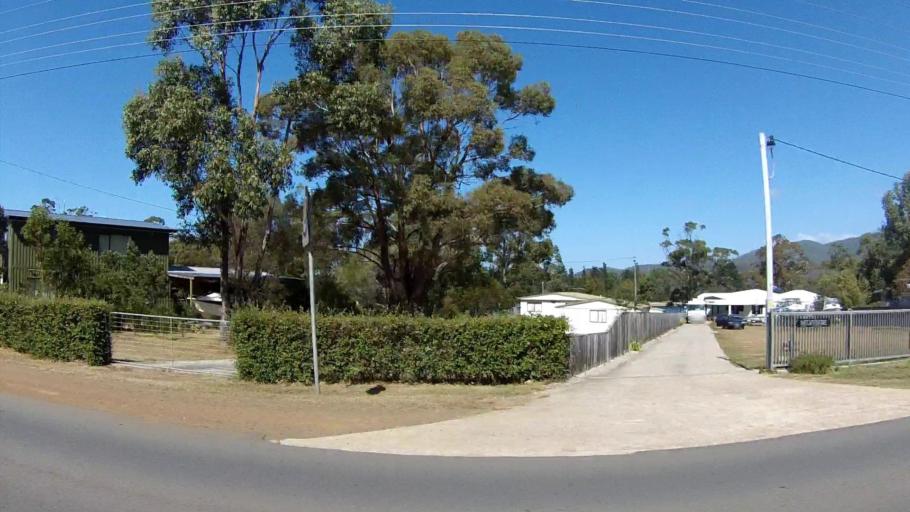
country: AU
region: Tasmania
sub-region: Sorell
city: Sorell
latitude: -42.5532
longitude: 147.8751
